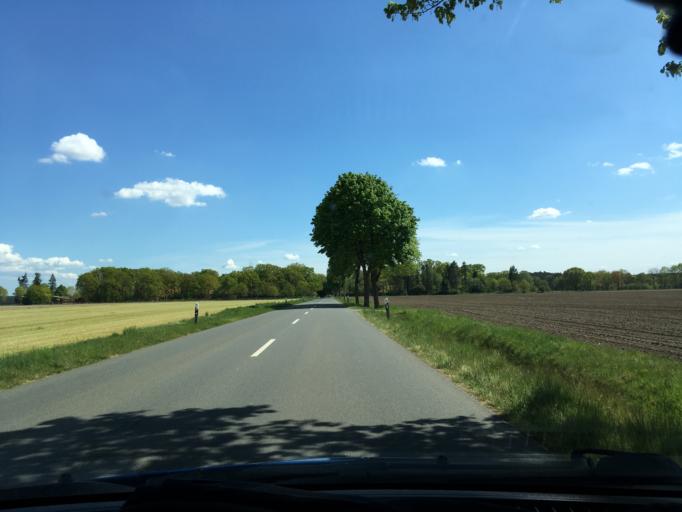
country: DE
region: Lower Saxony
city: Himbergen
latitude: 53.0887
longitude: 10.7364
